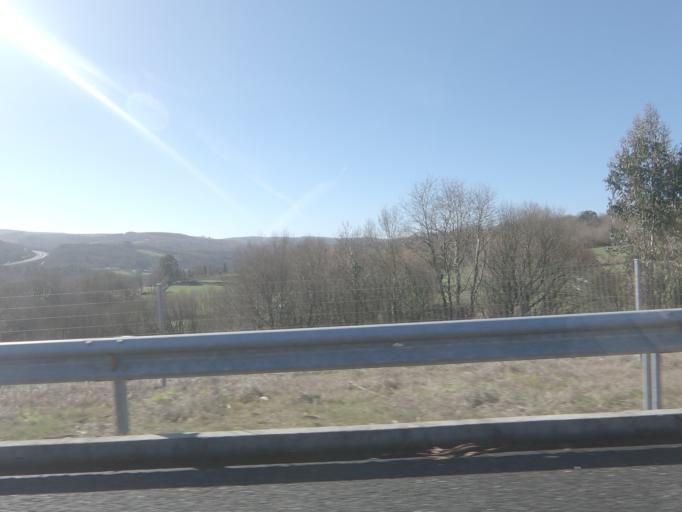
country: ES
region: Galicia
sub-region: Provincia de Pontevedra
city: Lalin
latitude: 42.6239
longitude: -8.1034
